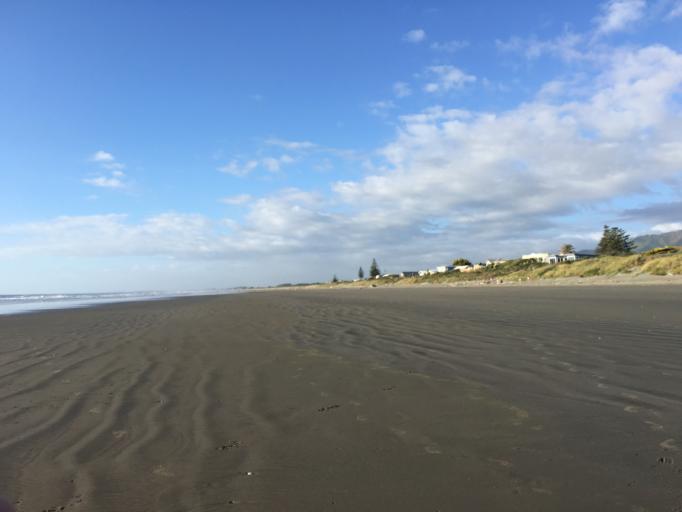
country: NZ
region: Wellington
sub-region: Kapiti Coast District
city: Paraparaumu
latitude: -40.8557
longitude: 175.0294
